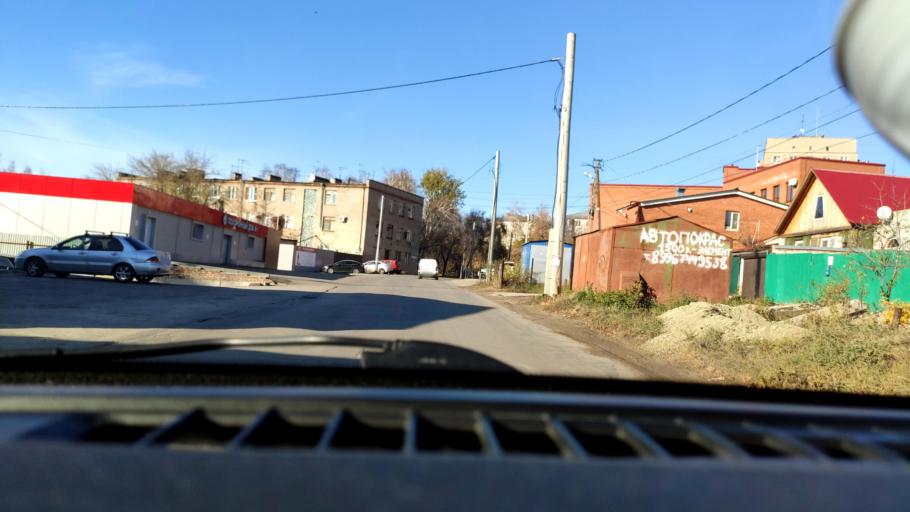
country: RU
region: Samara
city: Samara
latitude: 53.1858
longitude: 50.1781
